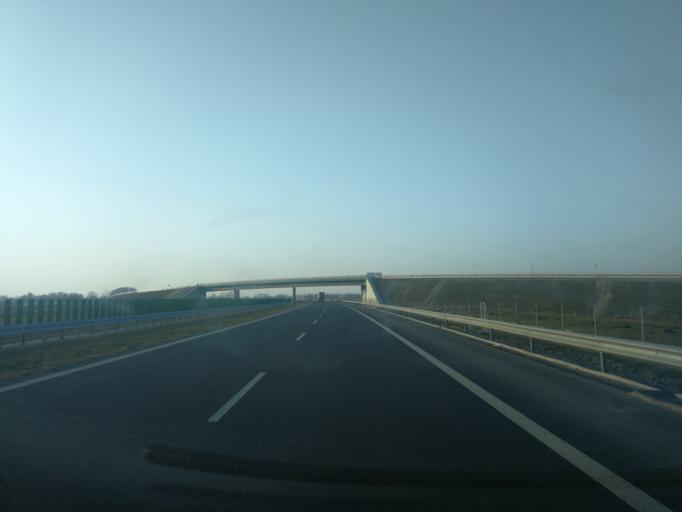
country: PL
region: Pomeranian Voivodeship
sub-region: Powiat nowodworski
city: Nowy Dwor Gdanski
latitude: 54.1865
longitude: 19.1720
